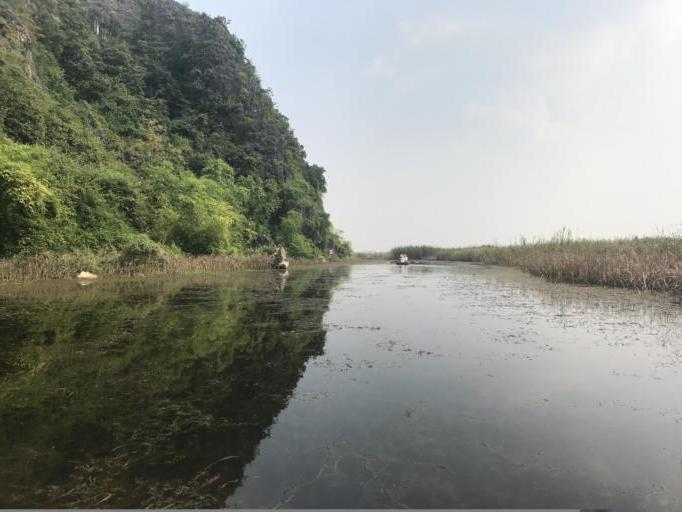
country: VN
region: Ninh Binh
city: Thi Tran Me
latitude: 20.3640
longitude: 105.8885
